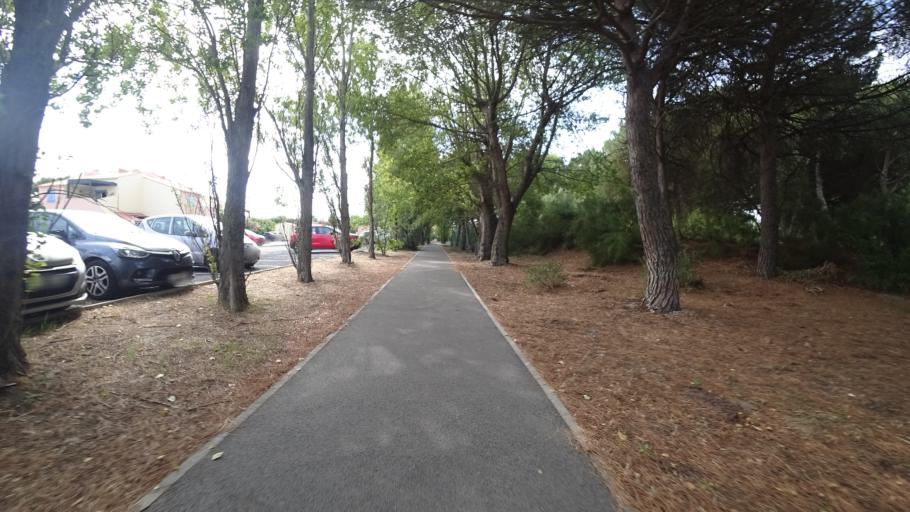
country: FR
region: Languedoc-Roussillon
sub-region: Departement de l'Aude
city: Leucate
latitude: 42.8526
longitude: 3.0371
